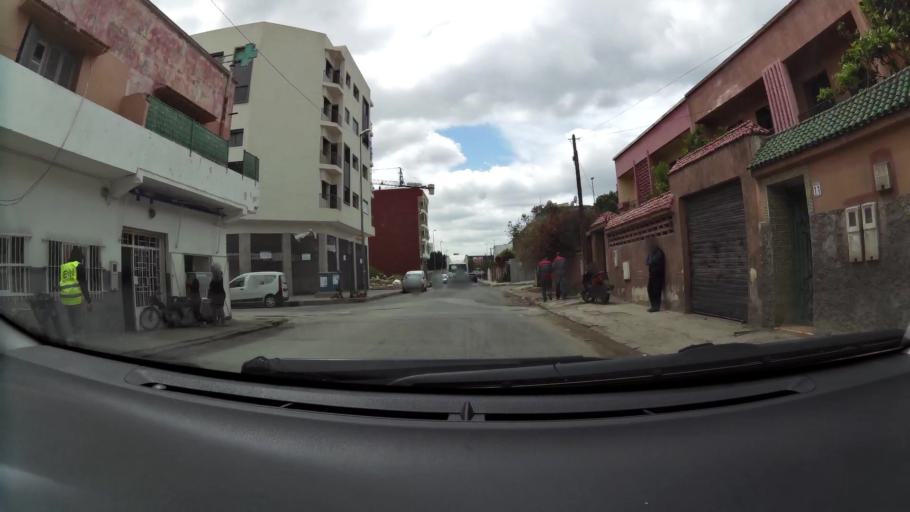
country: MA
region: Grand Casablanca
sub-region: Casablanca
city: Casablanca
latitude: 33.6064
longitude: -7.5484
